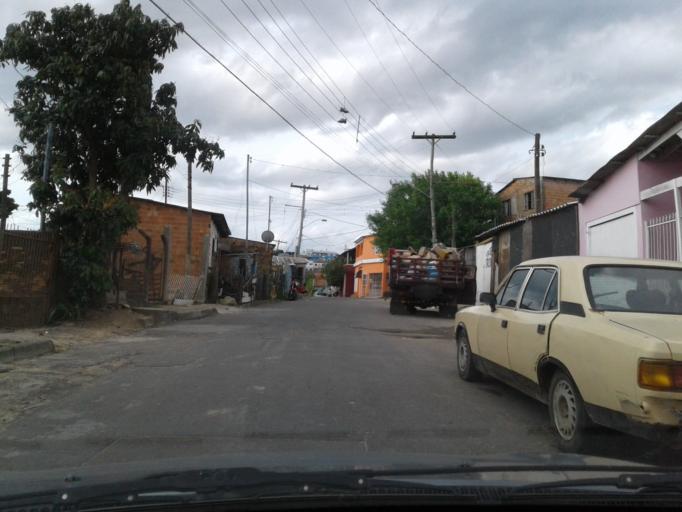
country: BR
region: Rio Grande do Sul
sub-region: Porto Alegre
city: Porto Alegre
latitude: -30.0494
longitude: -51.1520
